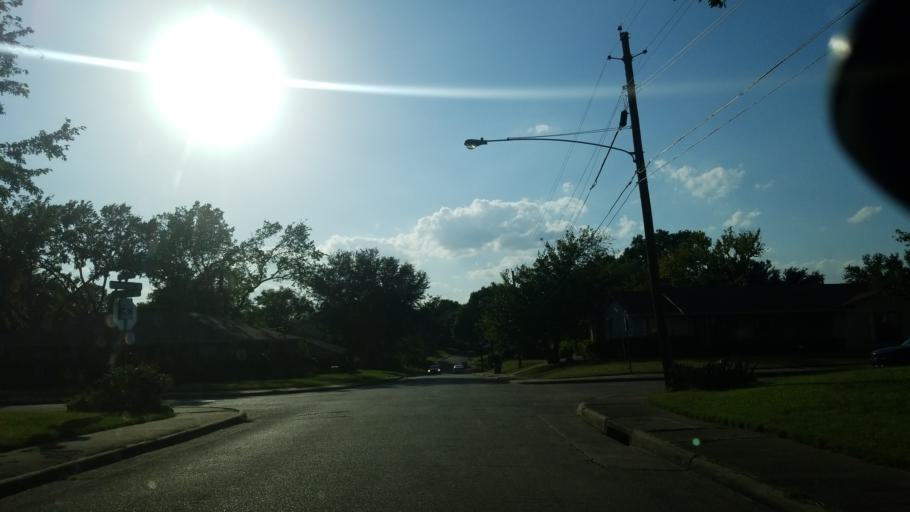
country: US
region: Texas
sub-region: Dallas County
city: Highland Park
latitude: 32.7836
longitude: -96.7114
